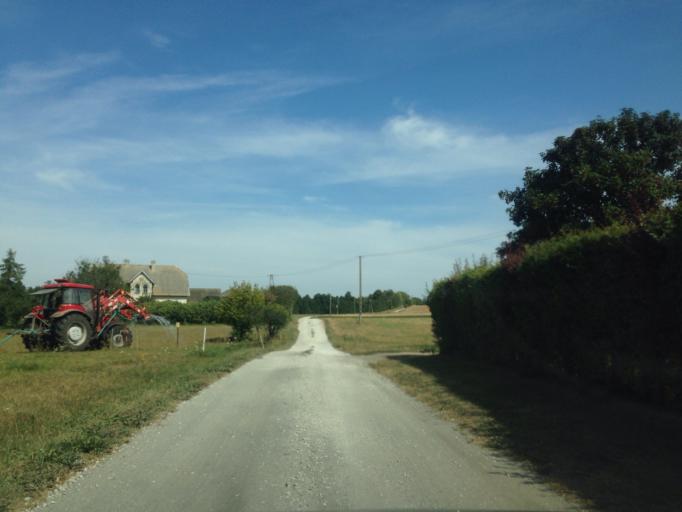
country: PL
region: Kujawsko-Pomorskie
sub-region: Powiat brodnicki
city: Bartniczka
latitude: 53.2326
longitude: 19.5668
